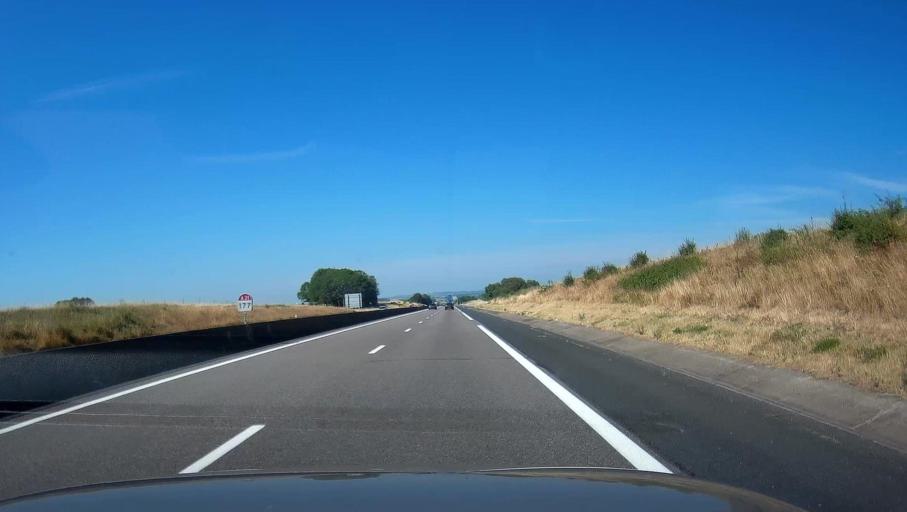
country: FR
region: Lorraine
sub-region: Departement des Vosges
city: Bulgneville
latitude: 48.2245
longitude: 5.8484
